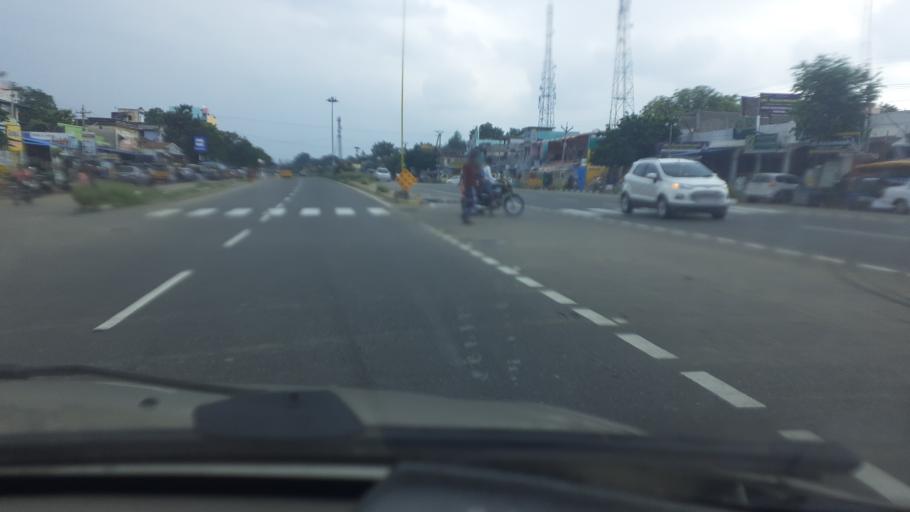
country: IN
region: Tamil Nadu
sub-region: Madurai
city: Kallupatti
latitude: 9.6990
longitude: 77.9722
